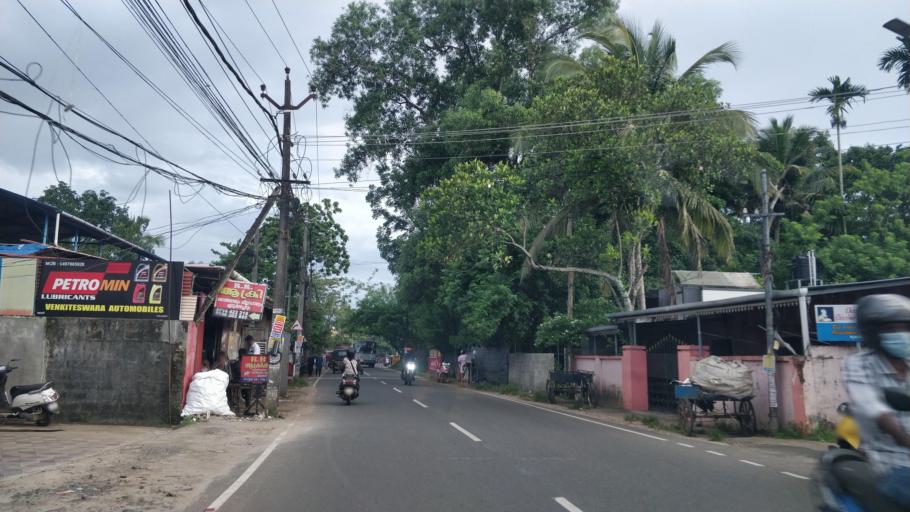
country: IN
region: Kerala
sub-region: Alappuzha
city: Alleppey
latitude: 9.5248
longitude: 76.3401
